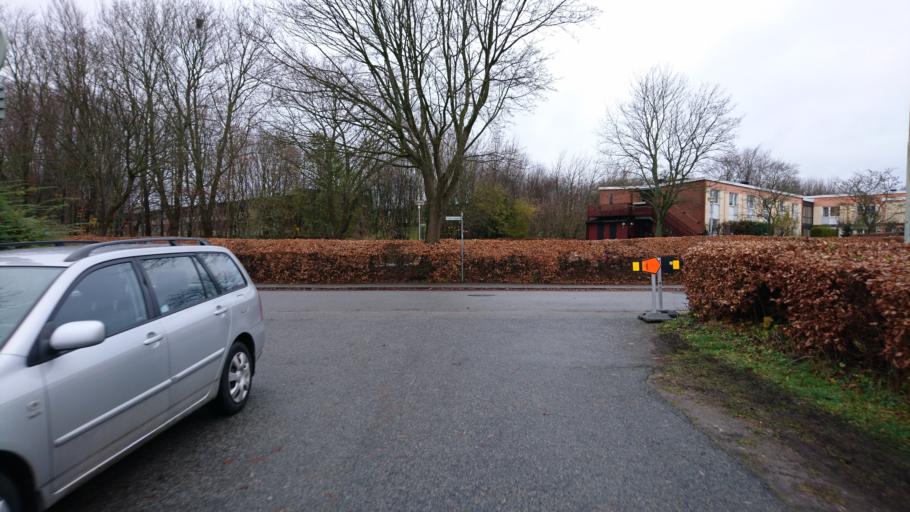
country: SE
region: Skane
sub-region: Lunds Kommun
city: Lund
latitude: 55.7070
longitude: 13.1671
